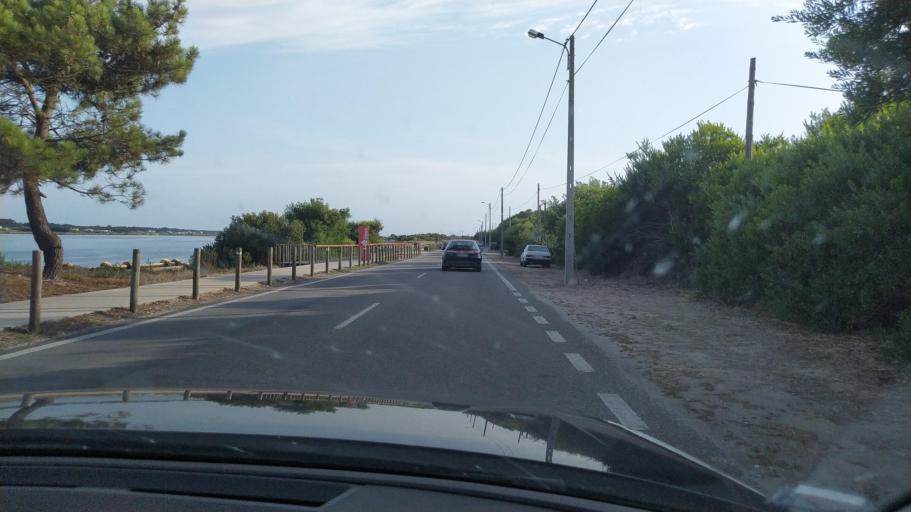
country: PT
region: Aveiro
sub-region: Ilhavo
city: Gafanha da Encarnacao
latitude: 40.5975
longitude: -8.7506
